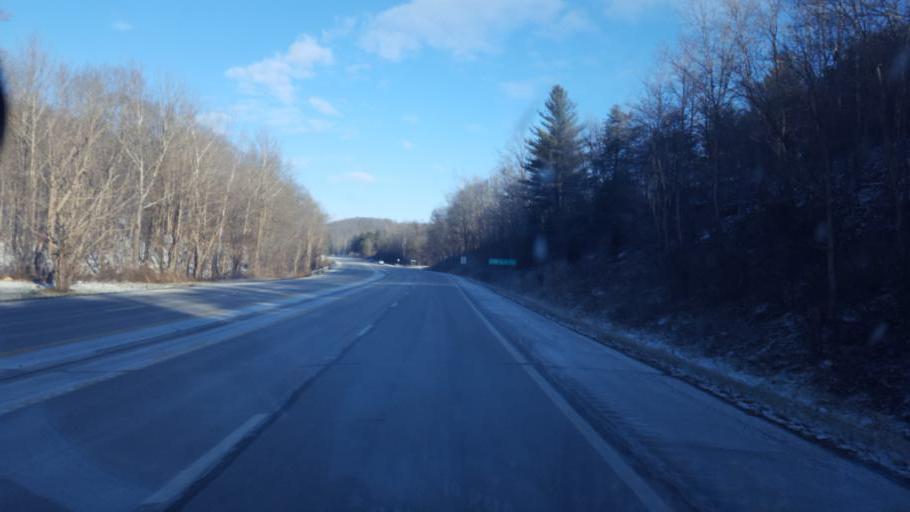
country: US
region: Ohio
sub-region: Pike County
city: Waverly
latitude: 39.1963
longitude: -82.9778
